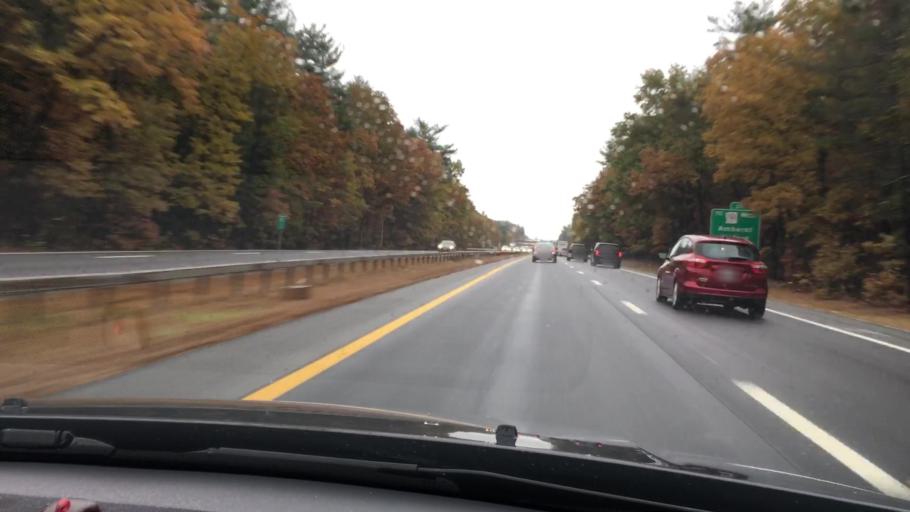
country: US
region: New Hampshire
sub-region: Hillsborough County
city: Nashua
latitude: 42.8001
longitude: -71.4980
